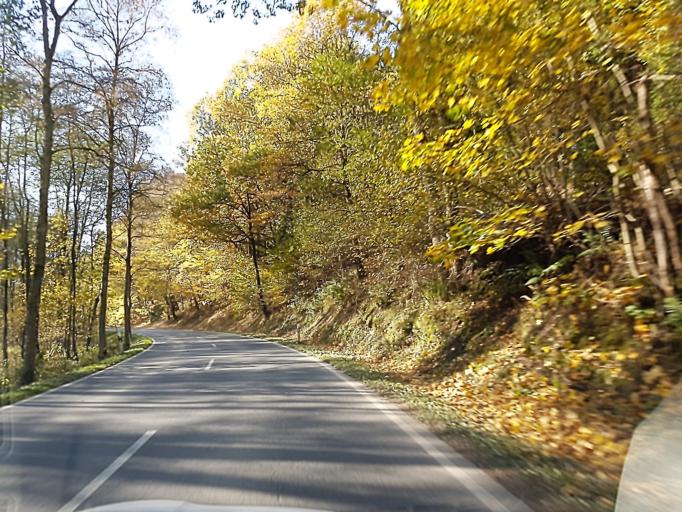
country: DE
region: North Rhine-Westphalia
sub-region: Regierungsbezirk Arnsberg
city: Drolshagen
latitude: 51.0778
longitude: 7.7446
